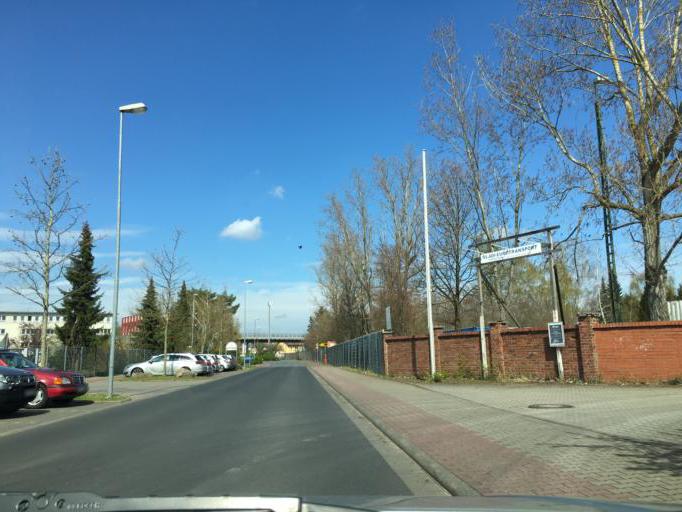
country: DE
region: Hesse
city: Heusenstamm
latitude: 50.0517
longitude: 8.8013
